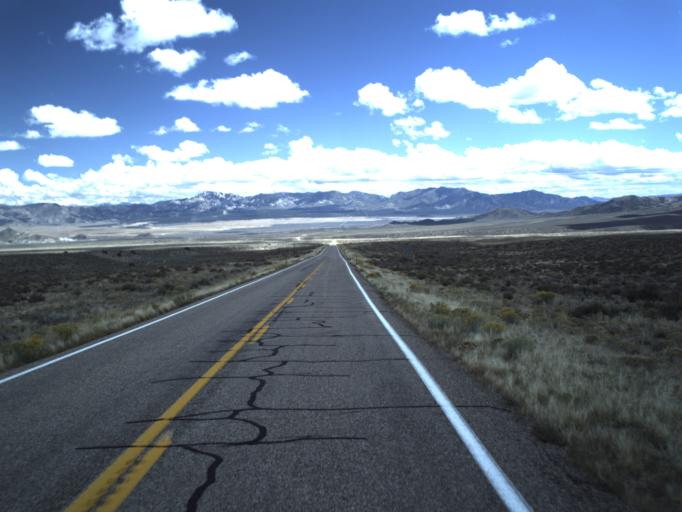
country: US
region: Utah
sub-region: Beaver County
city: Milford
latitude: 38.4556
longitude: -113.2158
